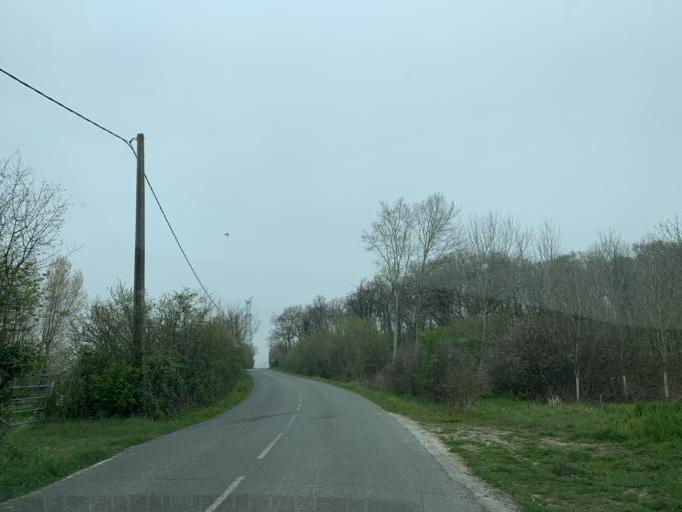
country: FR
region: Nord-Pas-de-Calais
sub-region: Departement du Pas-de-Calais
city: Rety
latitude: 50.7693
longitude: 1.7523
